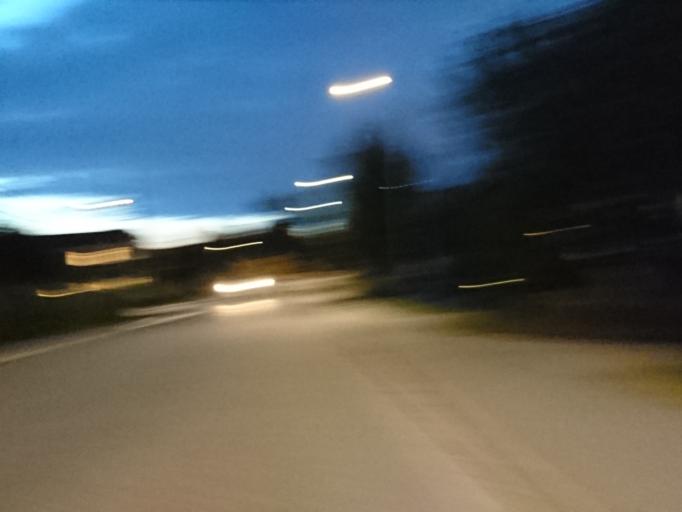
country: SE
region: Stockholm
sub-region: Huddinge Kommun
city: Segeltorp
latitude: 59.2781
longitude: 17.9400
